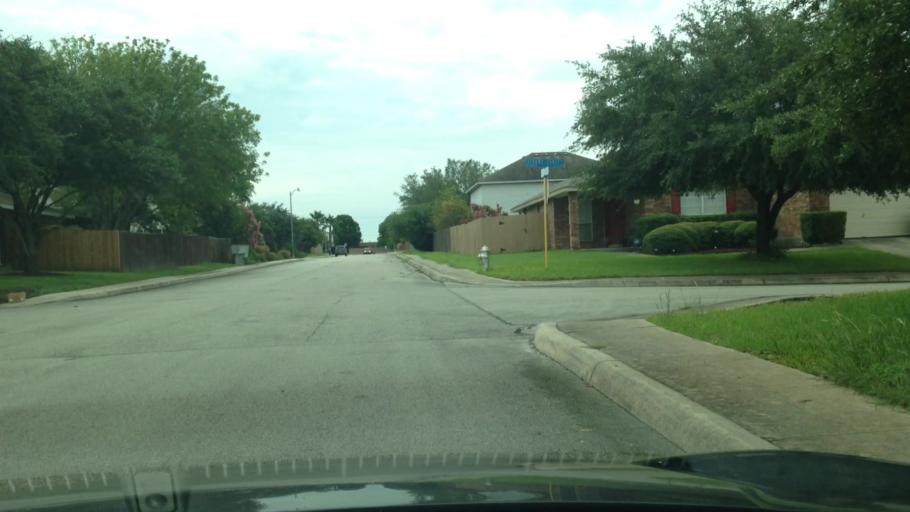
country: US
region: Texas
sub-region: Bexar County
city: Live Oak
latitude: 29.5854
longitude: -98.3878
